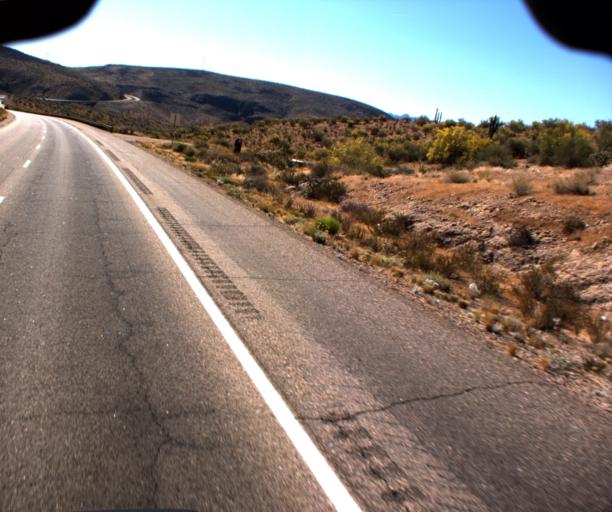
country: US
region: Arizona
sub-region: Yavapai County
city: Bagdad
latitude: 34.5857
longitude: -113.5061
